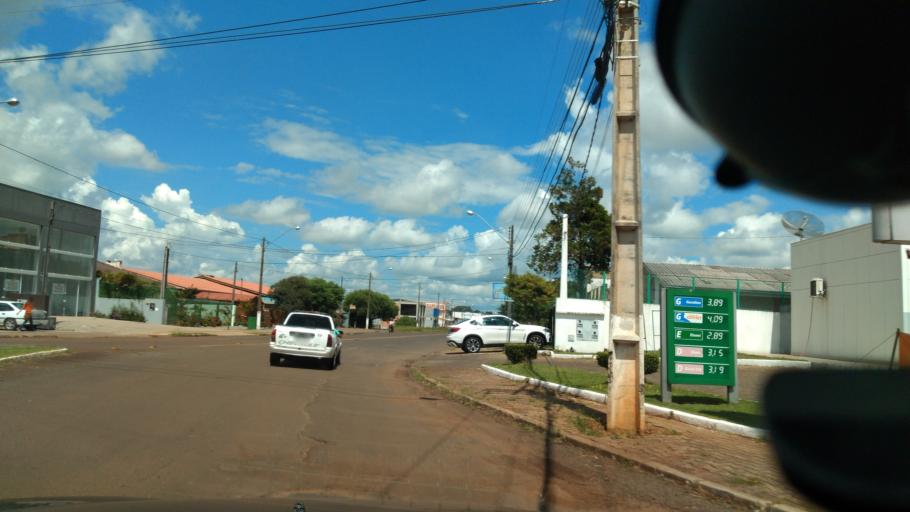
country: BR
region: Parana
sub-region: Guarapuava
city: Guarapuava
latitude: -25.3932
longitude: -51.4926
